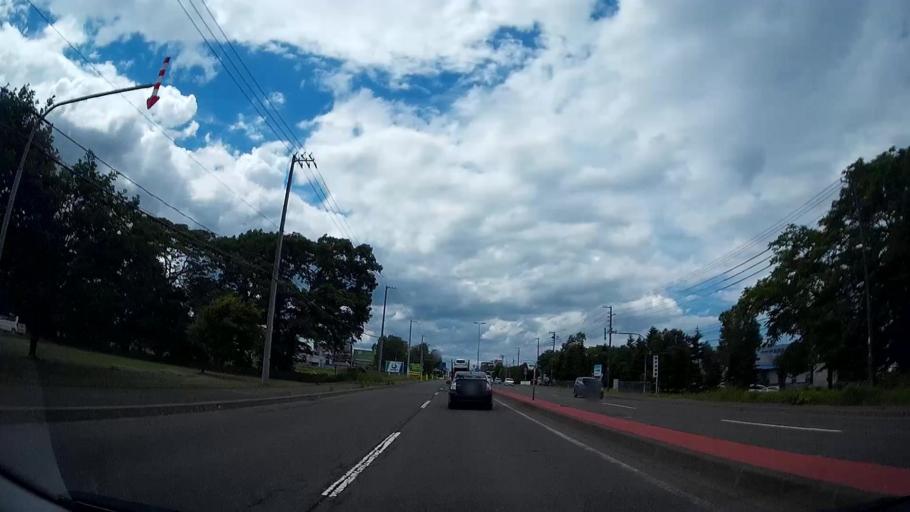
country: JP
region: Hokkaido
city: Chitose
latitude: 42.8674
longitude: 141.5921
